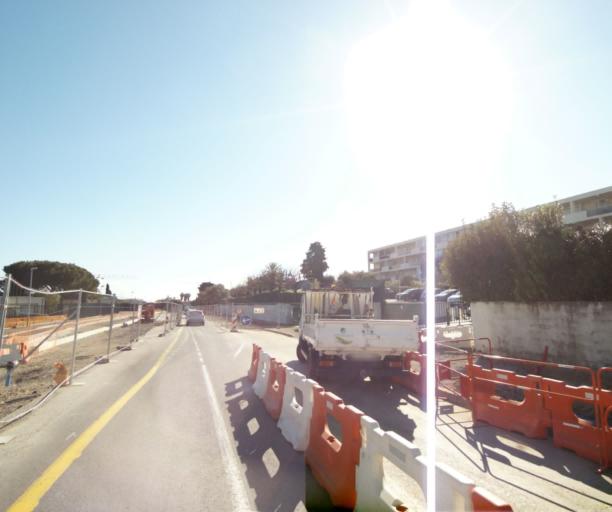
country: FR
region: Provence-Alpes-Cote d'Azur
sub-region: Departement des Alpes-Maritimes
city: Antibes
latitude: 43.5932
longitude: 7.1129
